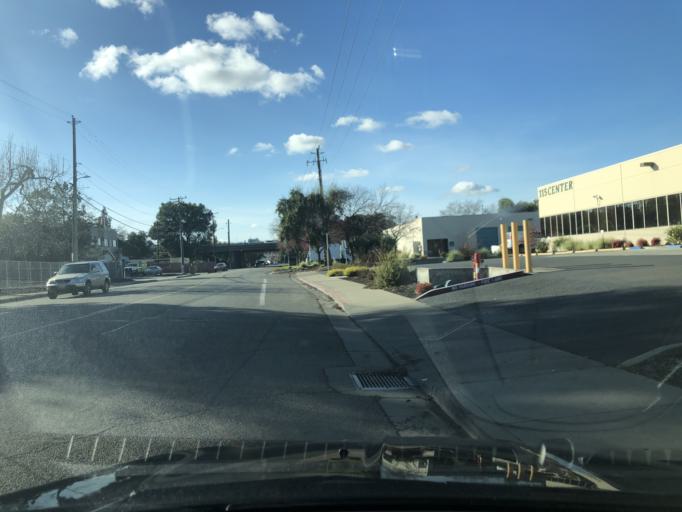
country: US
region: California
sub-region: Contra Costa County
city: Pacheco
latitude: 37.9840
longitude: -122.0639
